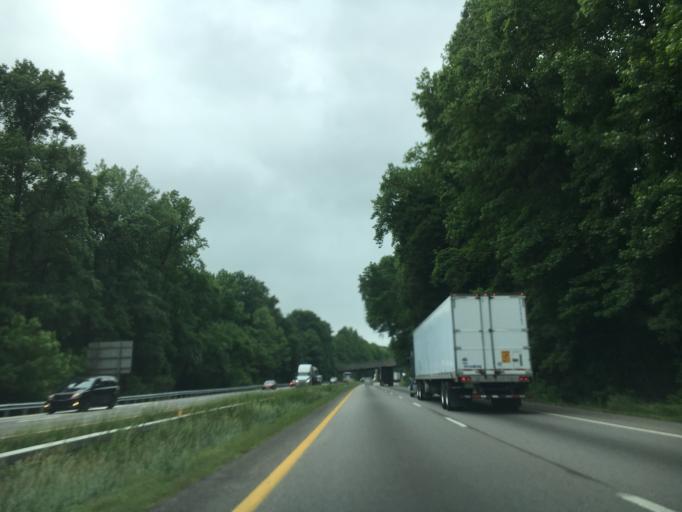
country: US
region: Virginia
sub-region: City of Petersburg
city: Petersburg
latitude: 37.2114
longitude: -77.4010
